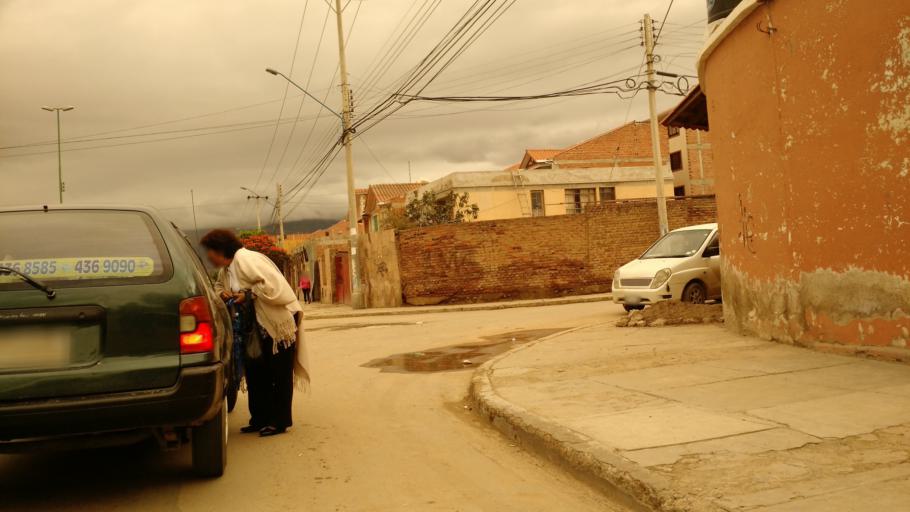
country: BO
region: Cochabamba
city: Cochabamba
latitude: -17.4213
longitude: -66.1665
